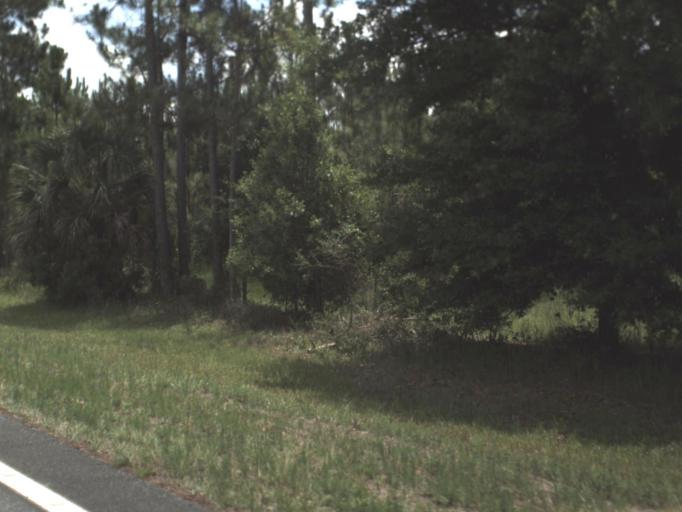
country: US
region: Florida
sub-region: Levy County
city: Chiefland
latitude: 29.2473
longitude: -82.9133
